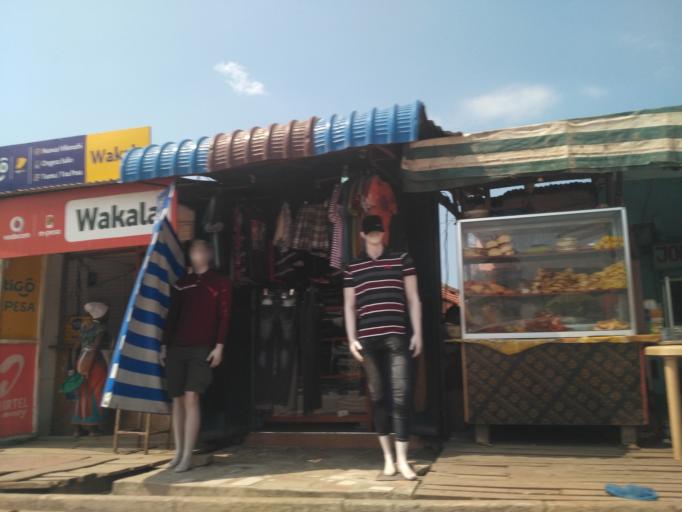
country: TZ
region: Dar es Salaam
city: Dar es Salaam
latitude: -6.8219
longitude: 39.3021
